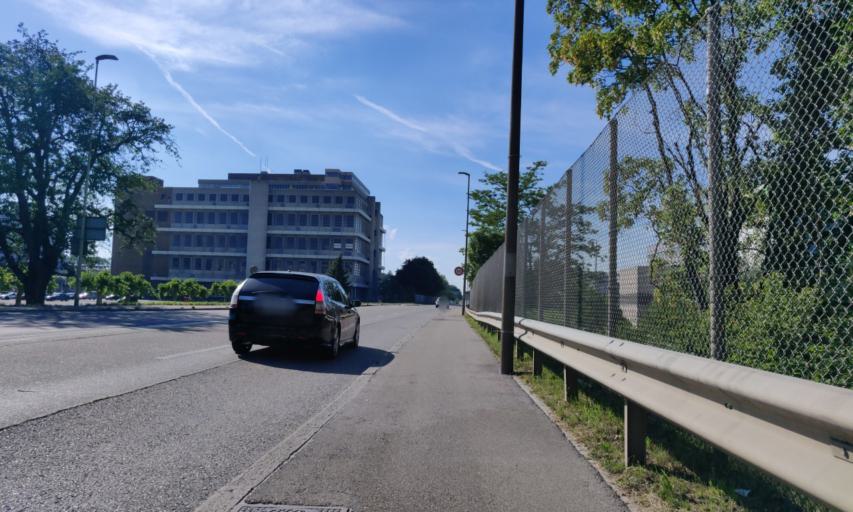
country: DE
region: Baden-Wuerttemberg
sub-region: Freiburg Region
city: Grenzach-Wyhlen
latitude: 47.5342
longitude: 7.6663
